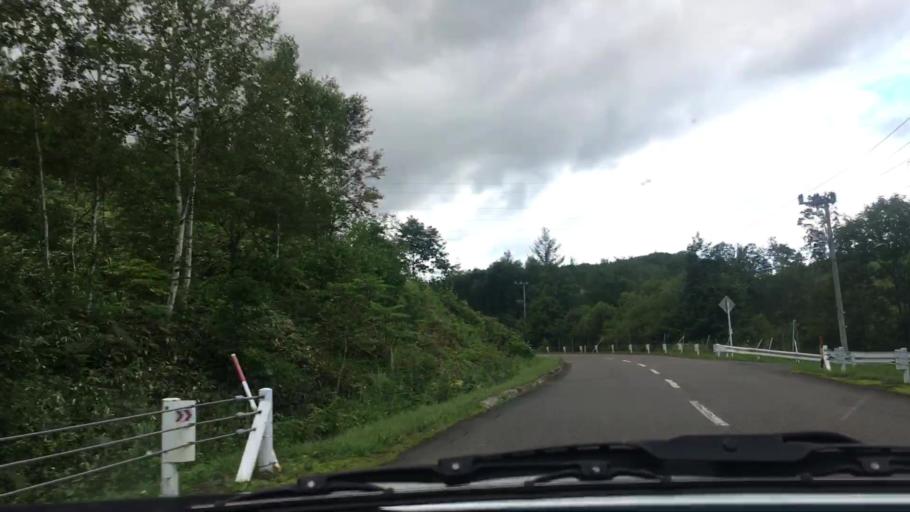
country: JP
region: Hokkaido
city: Otofuke
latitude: 43.1561
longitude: 142.8547
